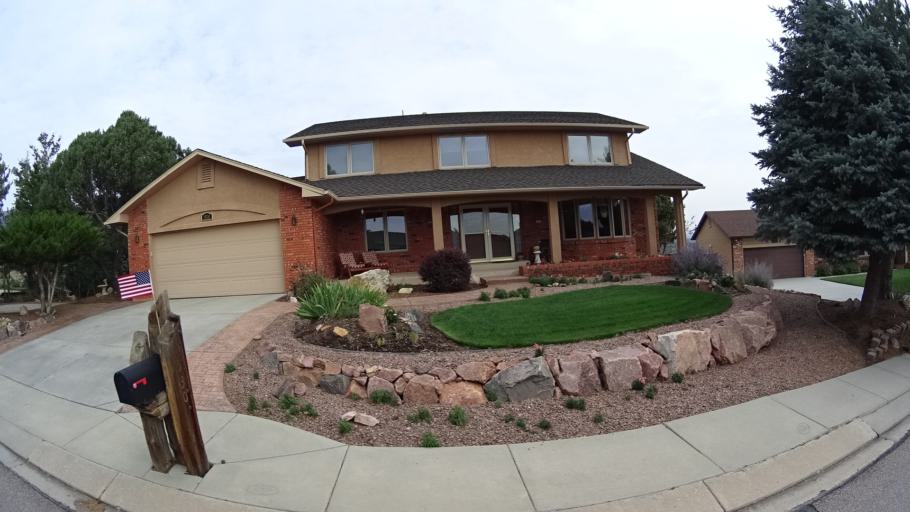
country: US
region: Colorado
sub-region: El Paso County
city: Air Force Academy
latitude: 38.9382
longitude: -104.8572
